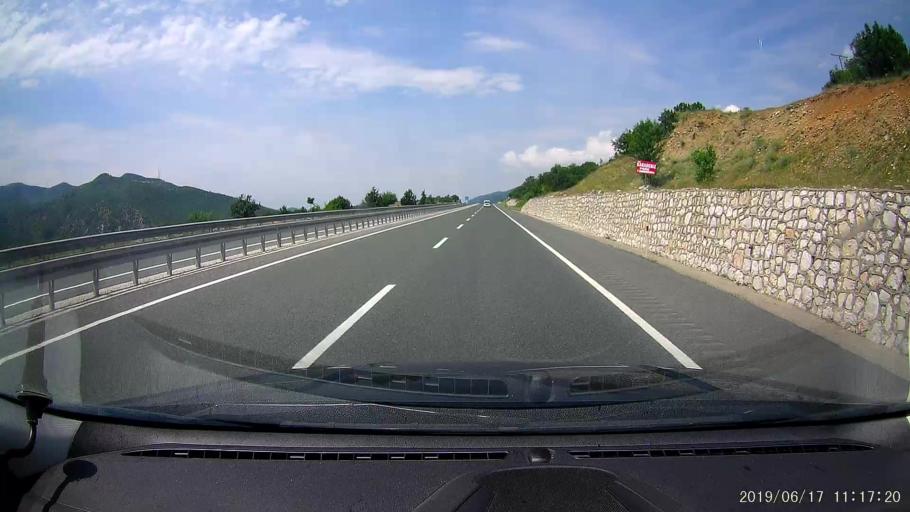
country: TR
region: Kastamonu
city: Tosya
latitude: 40.9421
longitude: 33.8776
